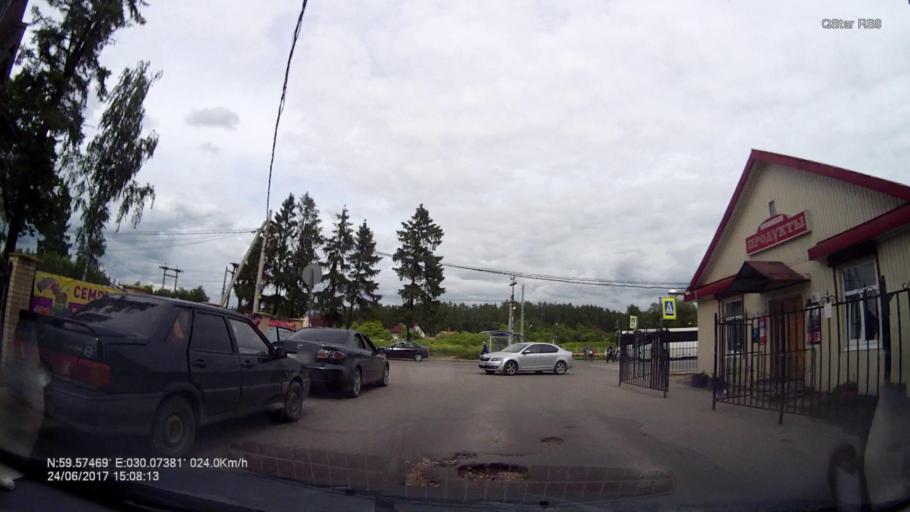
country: RU
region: Leningrad
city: Mariyenburg
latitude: 59.5747
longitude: 30.0739
